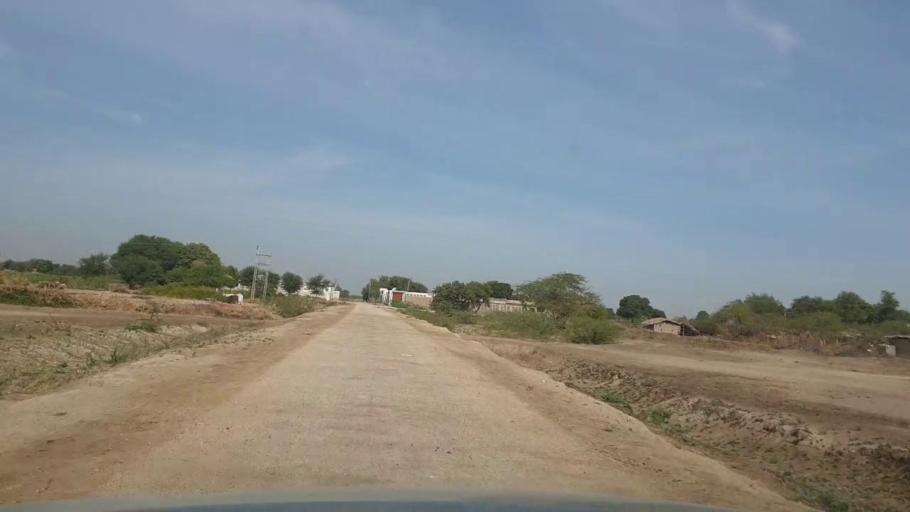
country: PK
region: Sindh
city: Nabisar
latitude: 25.1206
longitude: 69.6081
